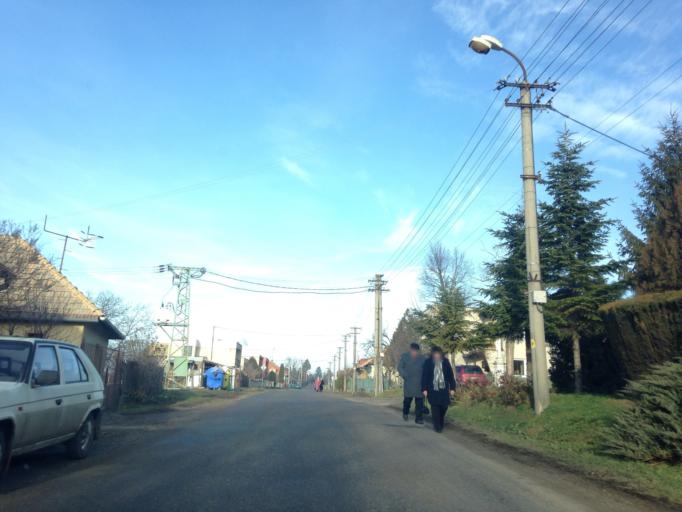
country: SK
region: Nitriansky
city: Svodin
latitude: 47.9061
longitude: 18.4131
